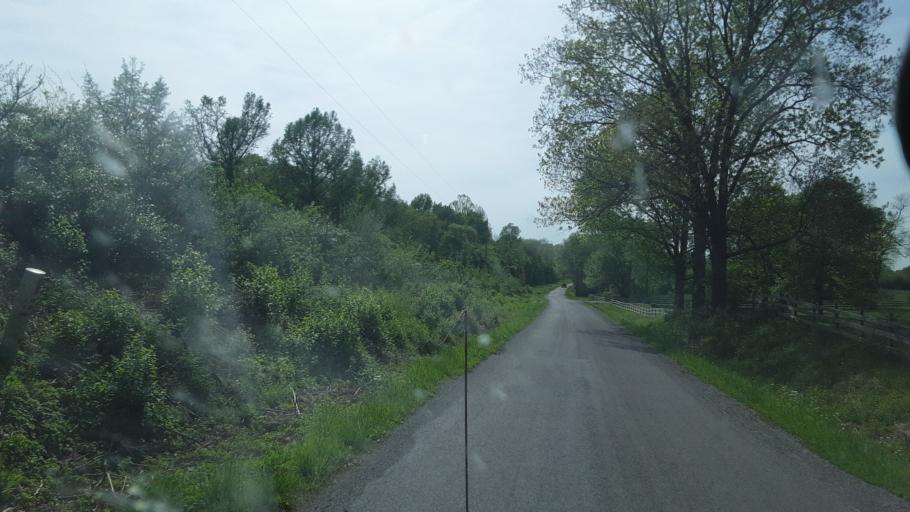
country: US
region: Illinois
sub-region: Jackson County
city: Carbondale
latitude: 37.6797
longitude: -89.2729
